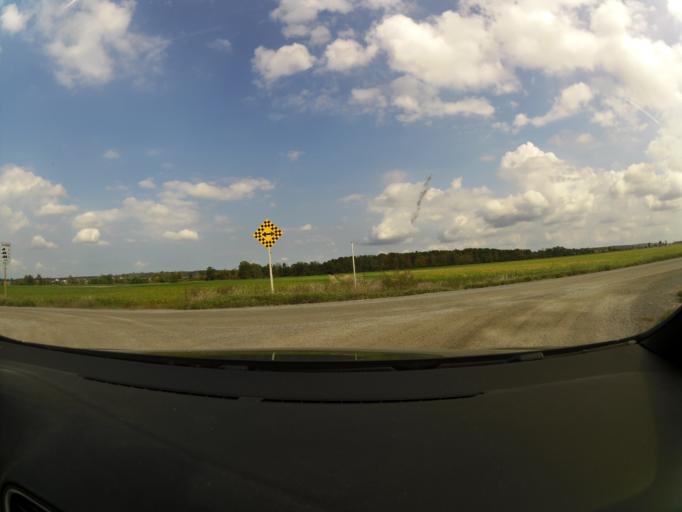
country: CA
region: Ontario
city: Arnprior
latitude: 45.3791
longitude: -76.1494
